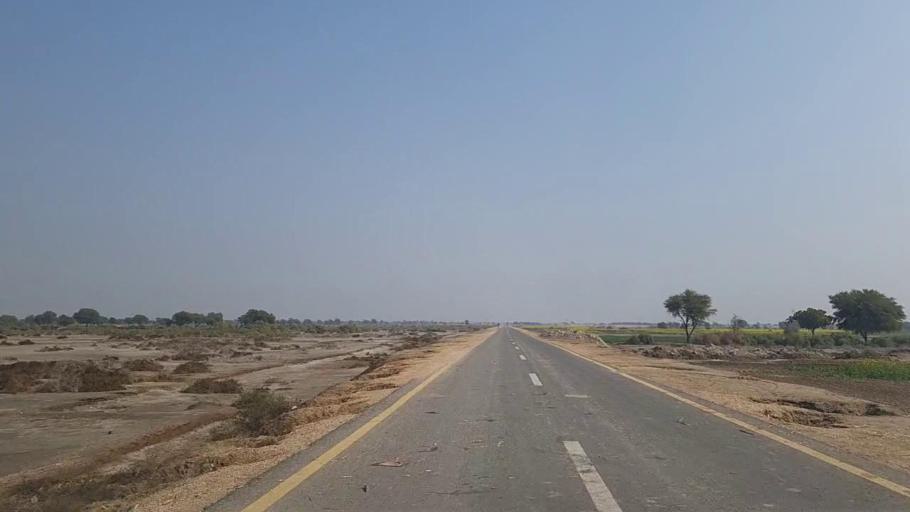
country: PK
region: Sindh
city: Jam Sahib
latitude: 26.3724
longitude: 68.5209
